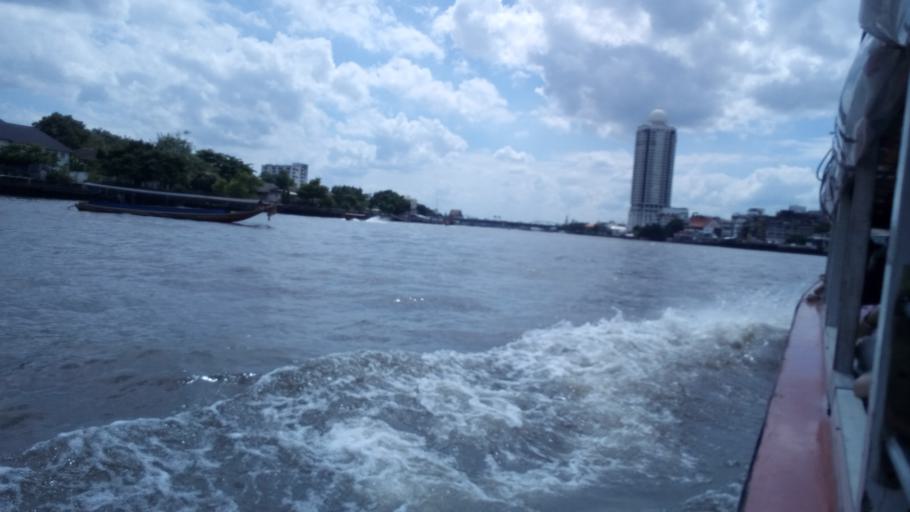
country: TH
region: Bangkok
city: Khlong San
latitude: 13.7361
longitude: 100.5085
